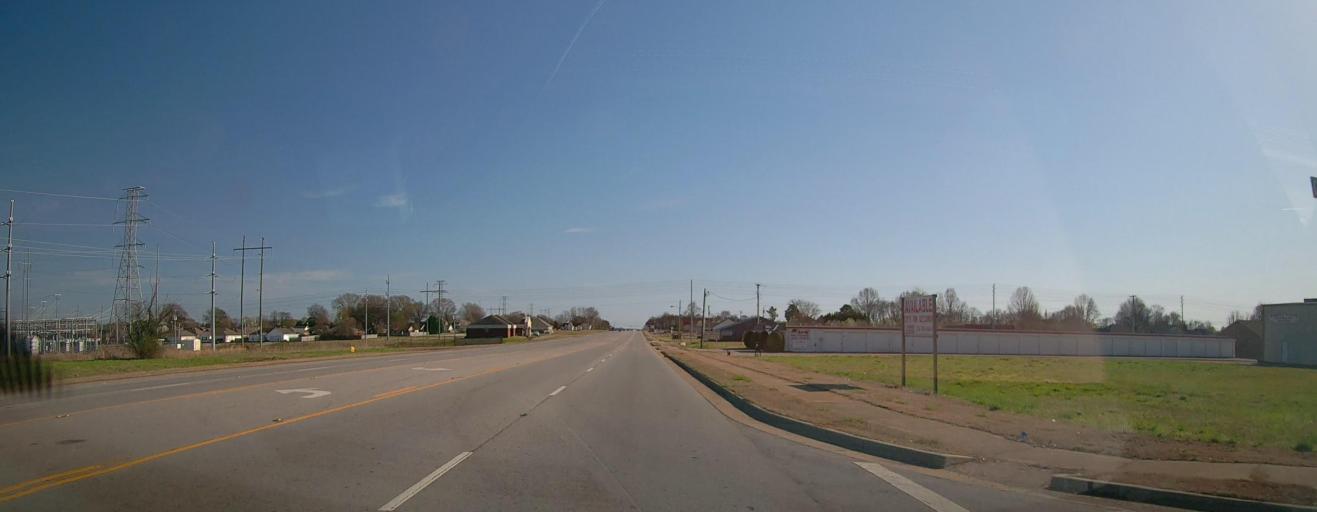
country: US
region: Alabama
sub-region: Colbert County
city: Muscle Shoals
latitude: 34.7389
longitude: -87.6353
